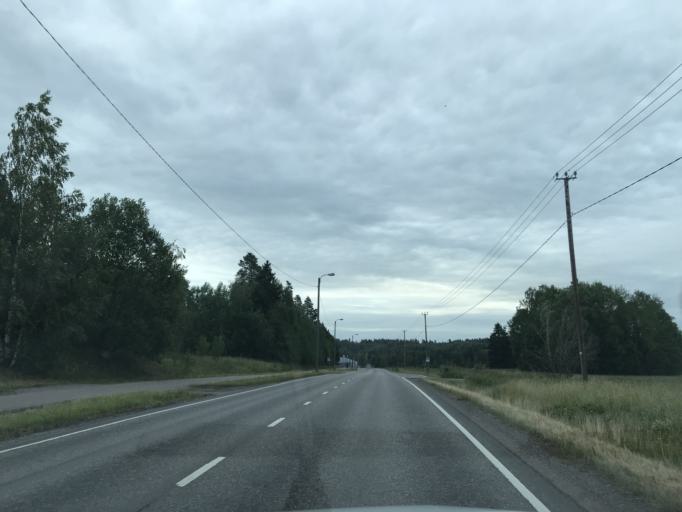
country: FI
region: Uusimaa
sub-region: Helsinki
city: Nurmijaervi
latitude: 60.3826
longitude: 24.7303
